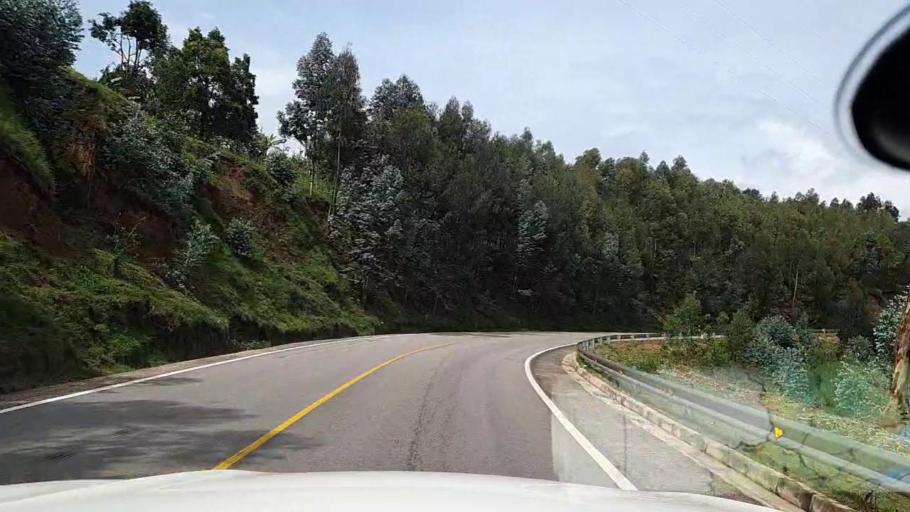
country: RW
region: Southern Province
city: Nzega
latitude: -2.5071
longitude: 29.5003
